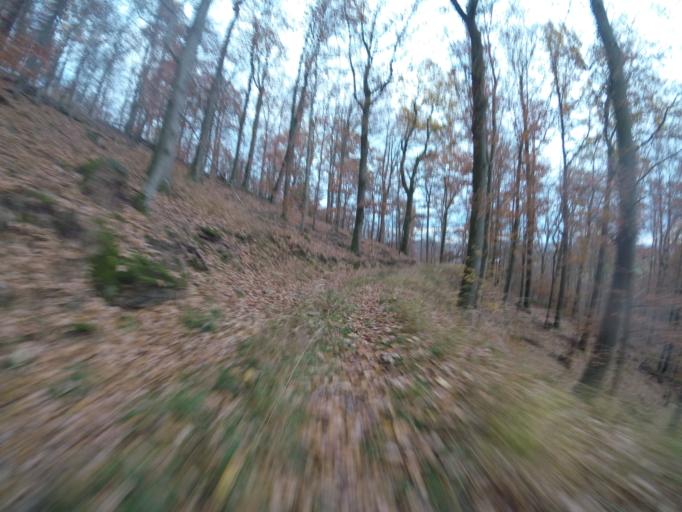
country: DE
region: Baden-Wuerttemberg
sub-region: Regierungsbezirk Stuttgart
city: Aspach
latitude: 49.0017
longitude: 9.3989
